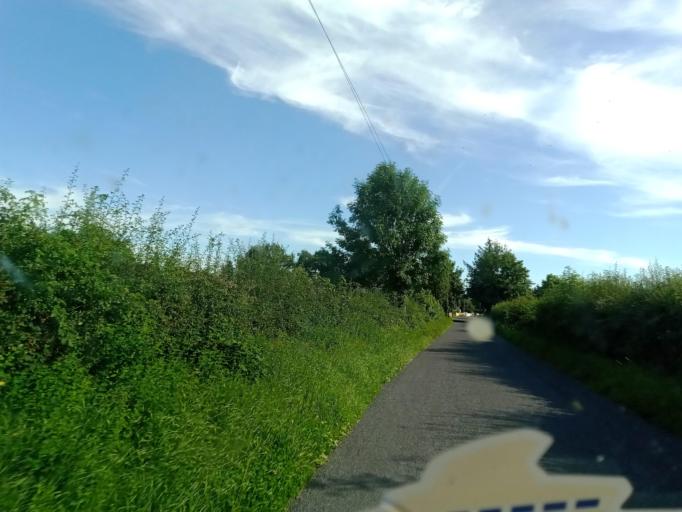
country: IE
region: Leinster
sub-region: Kilkenny
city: Ballyragget
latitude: 52.7744
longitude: -7.3883
